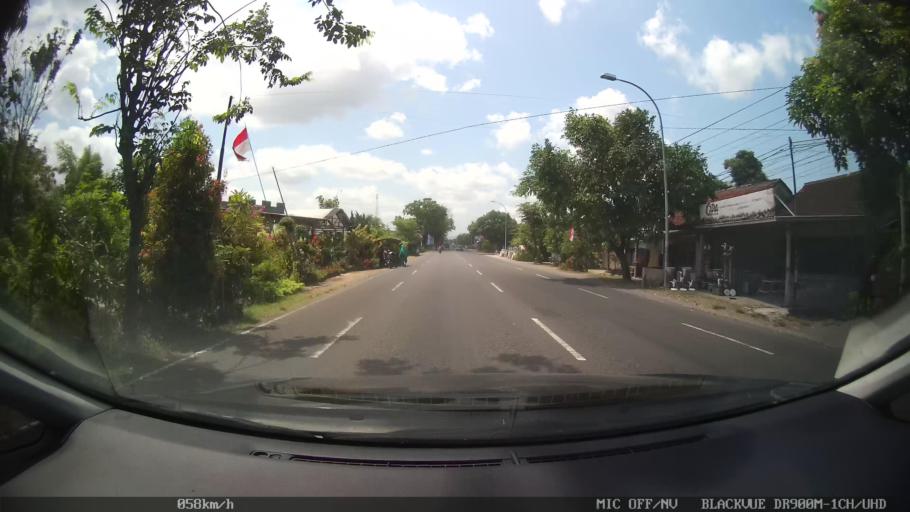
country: ID
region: Daerah Istimewa Yogyakarta
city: Pandak
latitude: -7.9072
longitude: 110.3059
